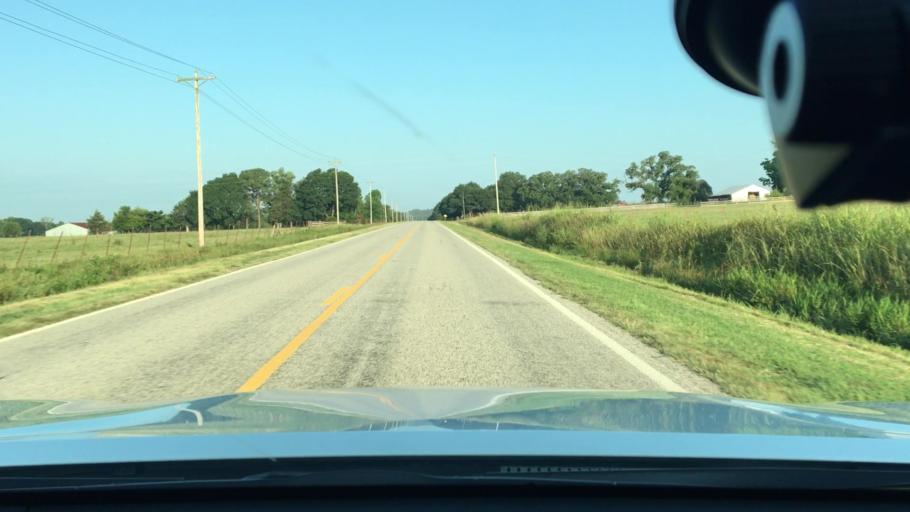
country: US
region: Arkansas
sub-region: Johnson County
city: Coal Hill
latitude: 35.3507
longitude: -93.5717
